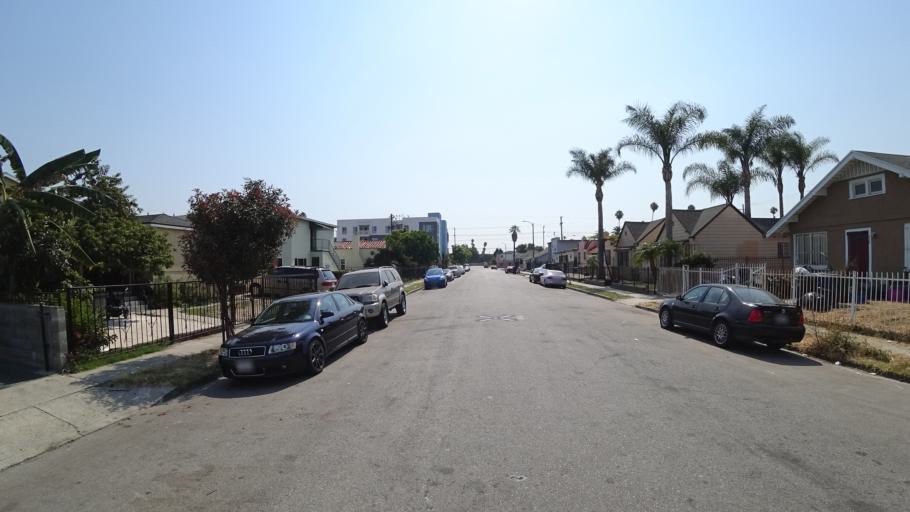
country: US
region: California
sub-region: Los Angeles County
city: Westmont
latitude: 33.9698
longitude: -118.2842
